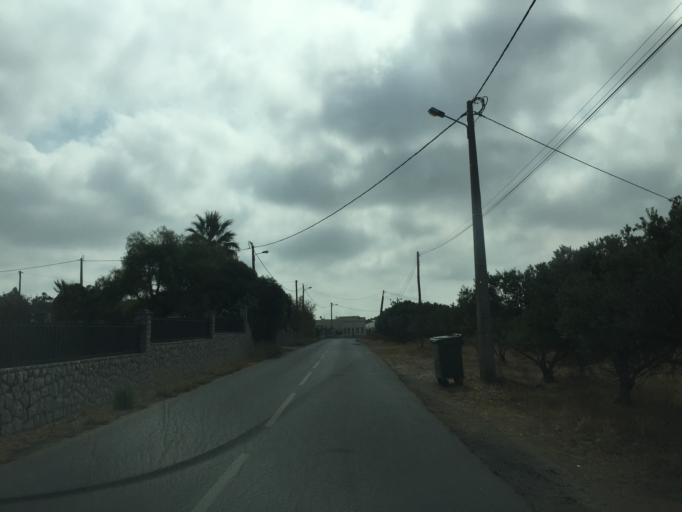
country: PT
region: Faro
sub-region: Olhao
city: Olhao
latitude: 37.0719
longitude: -7.8849
